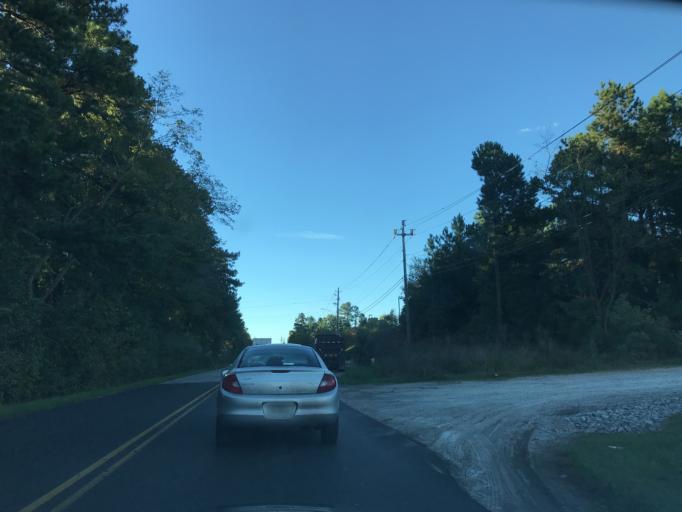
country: US
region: North Carolina
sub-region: Wake County
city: Morrisville
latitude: 35.8412
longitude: -78.8327
